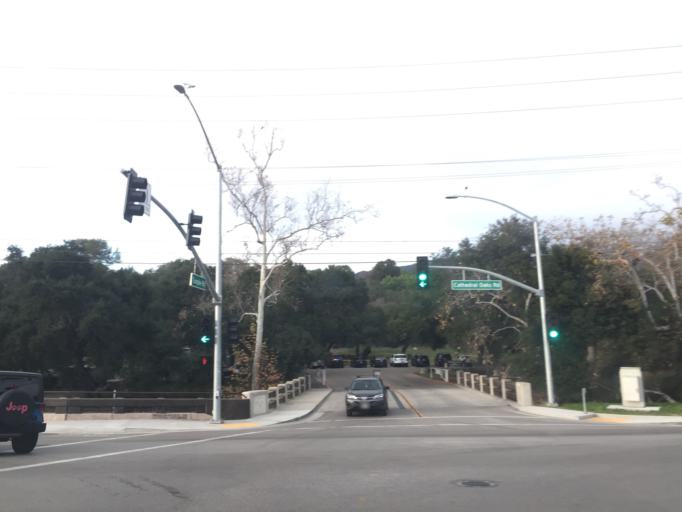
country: US
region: California
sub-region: Santa Barbara County
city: Goleta
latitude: 34.4512
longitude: -119.7901
